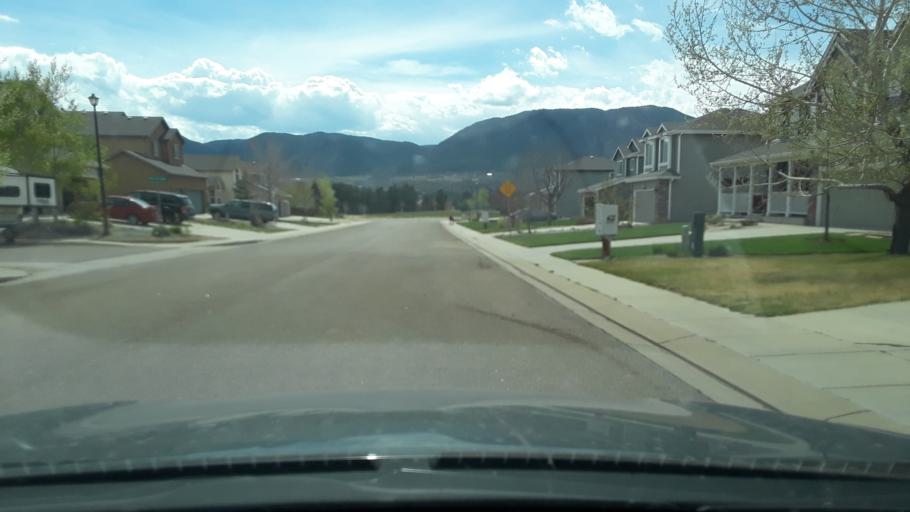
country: US
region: Colorado
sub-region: El Paso County
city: Monument
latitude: 39.0791
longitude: -104.8670
